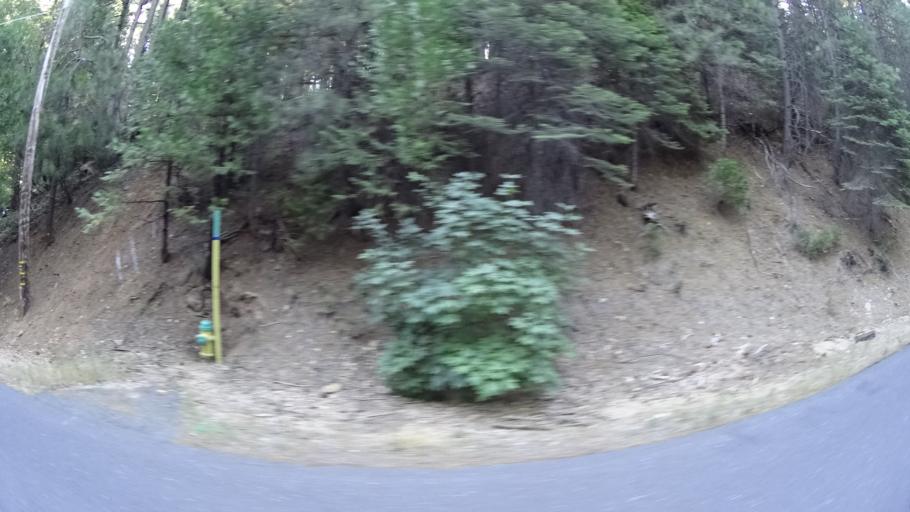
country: US
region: California
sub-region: Calaveras County
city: Arnold
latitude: 38.2637
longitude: -120.3174
